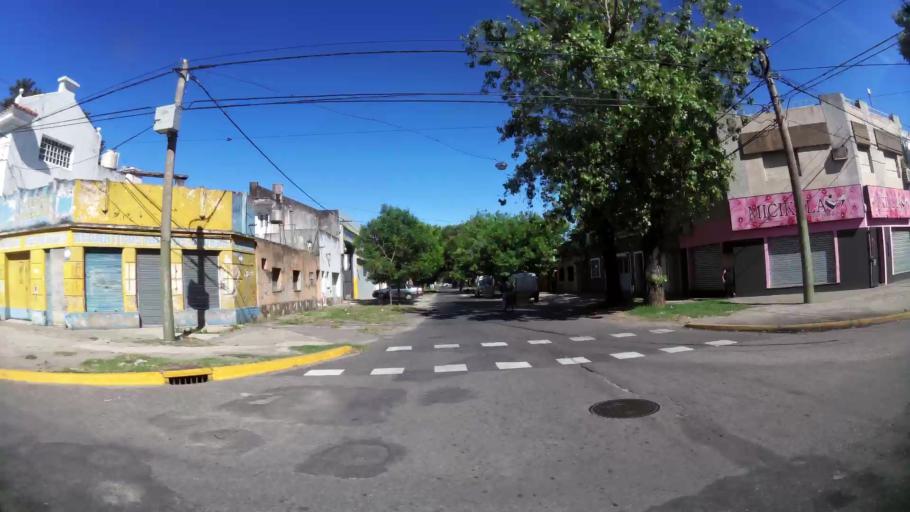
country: AR
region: Santa Fe
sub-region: Departamento de Rosario
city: Rosario
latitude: -32.9512
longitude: -60.6823
